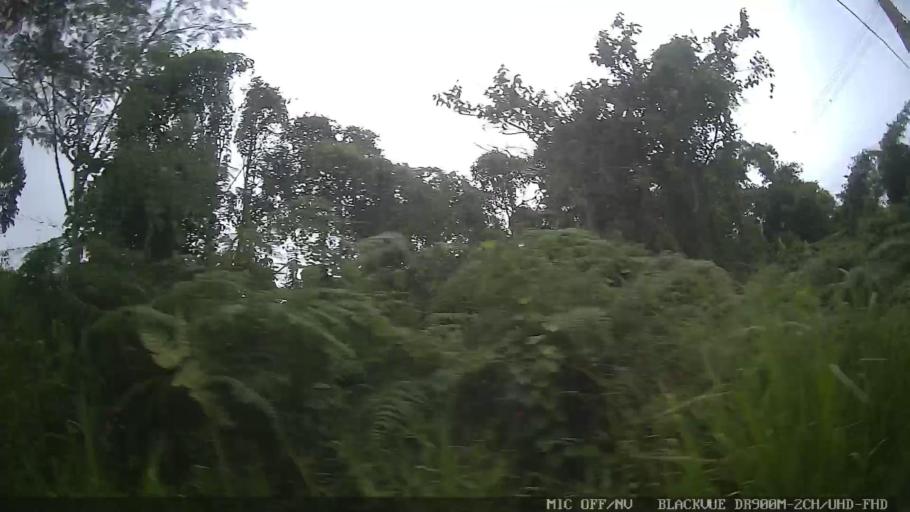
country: BR
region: Sao Paulo
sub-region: Mogi das Cruzes
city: Mogi das Cruzes
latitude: -23.5370
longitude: -46.1295
